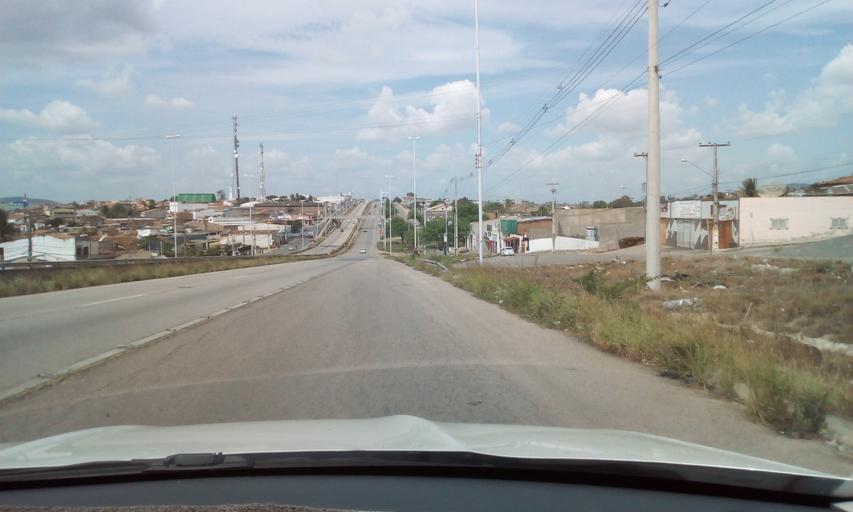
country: BR
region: Pernambuco
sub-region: Bezerros
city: Bezerros
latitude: -8.2468
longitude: -35.7576
